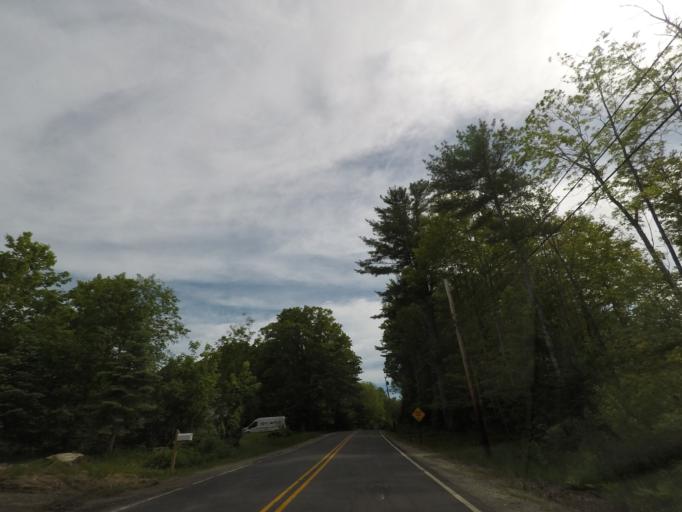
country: US
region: Maine
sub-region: Sagadahoc County
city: Richmond
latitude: 44.1196
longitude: -69.7762
